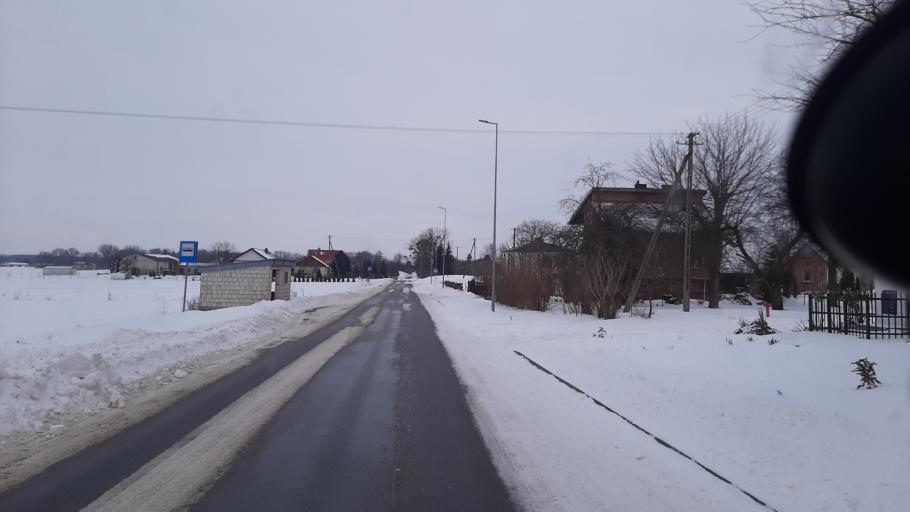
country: PL
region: Lublin Voivodeship
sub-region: Powiat lubelski
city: Garbow
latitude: 51.3266
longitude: 22.3273
